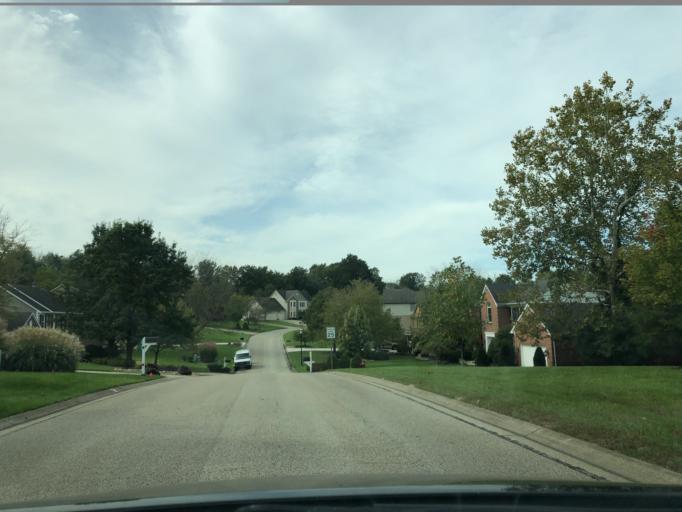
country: US
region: Ohio
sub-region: Hamilton County
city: Loveland
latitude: 39.2460
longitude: -84.2693
